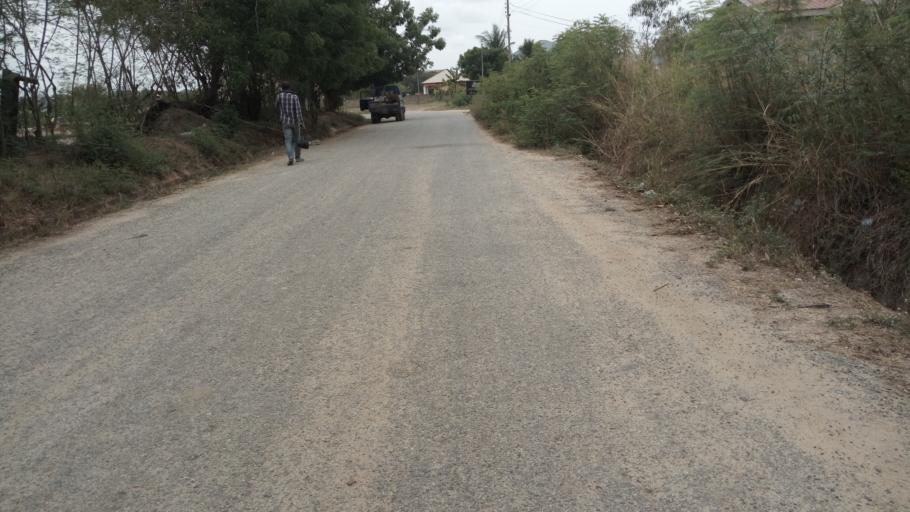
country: GH
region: Central
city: Winneba
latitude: 5.3802
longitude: -0.6407
